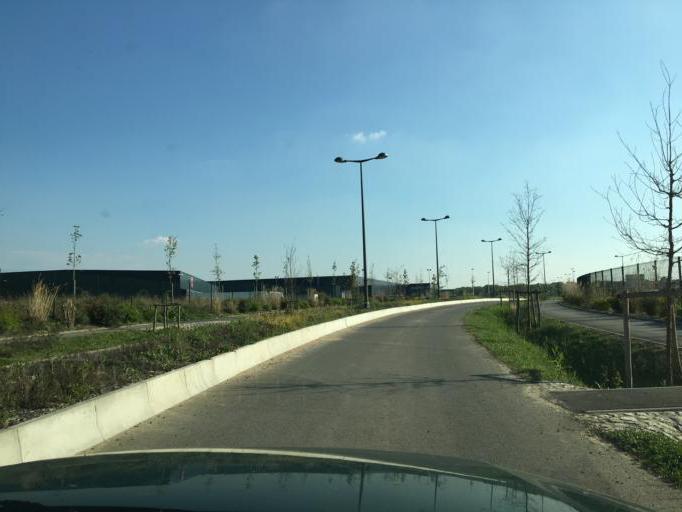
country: FR
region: Centre
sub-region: Departement du Loiret
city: Gidy
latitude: 47.9651
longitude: 1.8485
